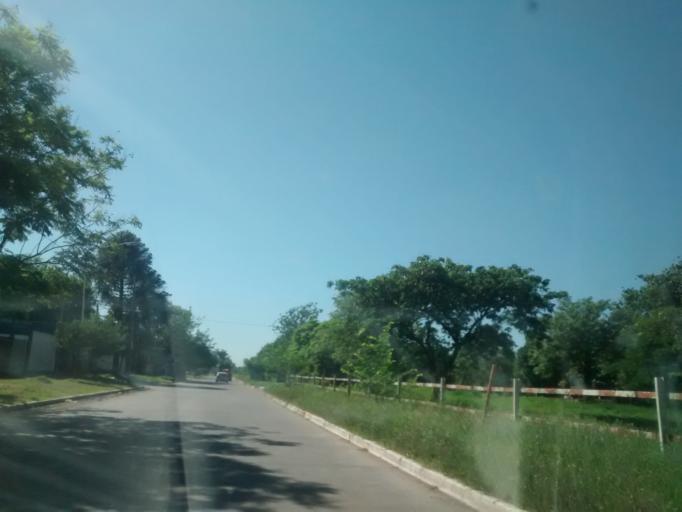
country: AR
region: Chaco
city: Resistencia
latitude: -27.4450
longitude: -59.0021
